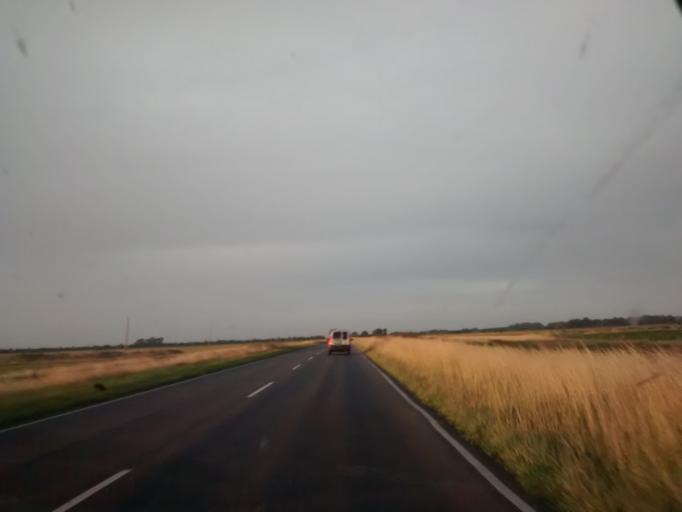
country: AR
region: Buenos Aires
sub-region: Partido de General Belgrano
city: General Belgrano
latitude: -35.9082
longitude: -58.6191
